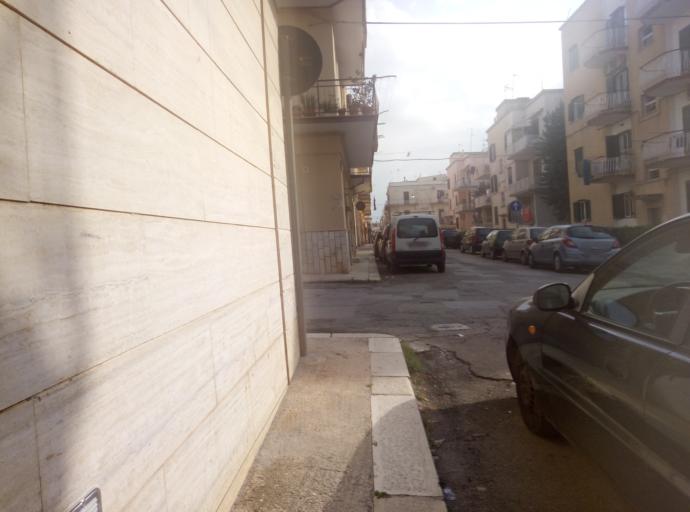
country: IT
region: Apulia
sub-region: Provincia di Bari
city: Ruvo di Puglia
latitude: 41.1218
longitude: 16.4860
